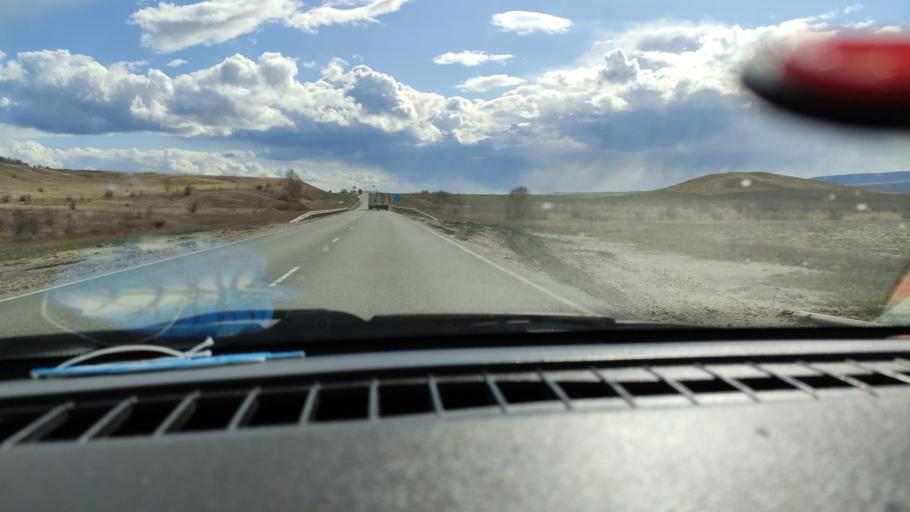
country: RU
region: Saratov
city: Alekseyevka
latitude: 52.3485
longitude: 47.9382
